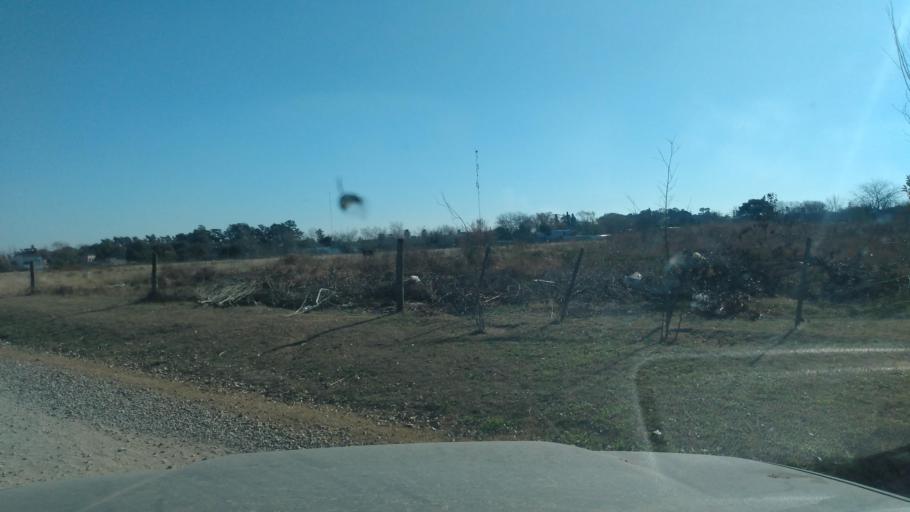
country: AR
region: Buenos Aires
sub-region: Partido de Lujan
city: Lujan
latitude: -34.5653
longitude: -59.0843
